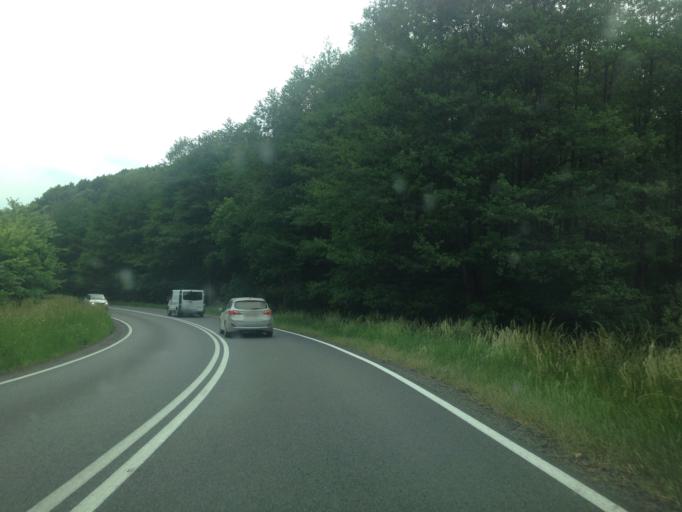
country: PL
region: Kujawsko-Pomorskie
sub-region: Powiat grudziadzki
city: Rogozno
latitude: 53.5091
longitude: 18.9260
